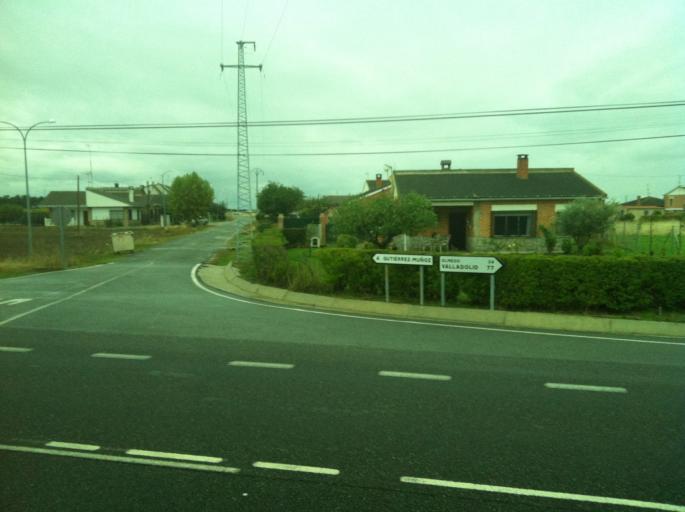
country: ES
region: Castille and Leon
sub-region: Provincia de Segovia
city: Martin Munoz de las Posadas
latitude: 40.9948
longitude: -4.5996
